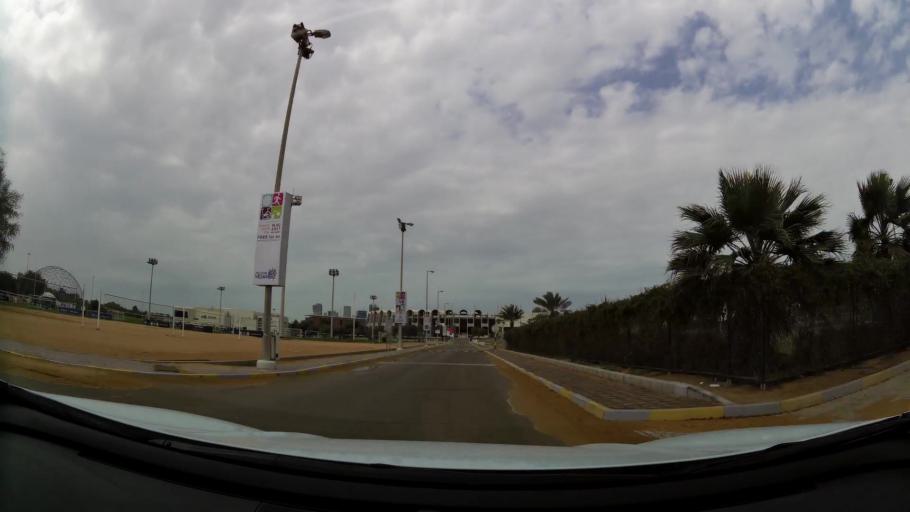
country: AE
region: Abu Dhabi
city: Abu Dhabi
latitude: 24.4135
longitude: 54.4576
